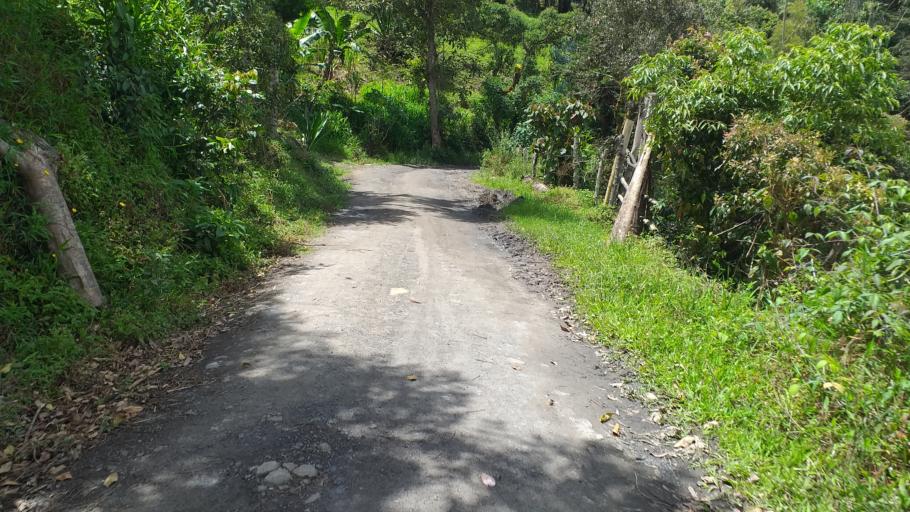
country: CO
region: Cundinamarca
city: Tenza
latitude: 5.1169
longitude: -73.4613
